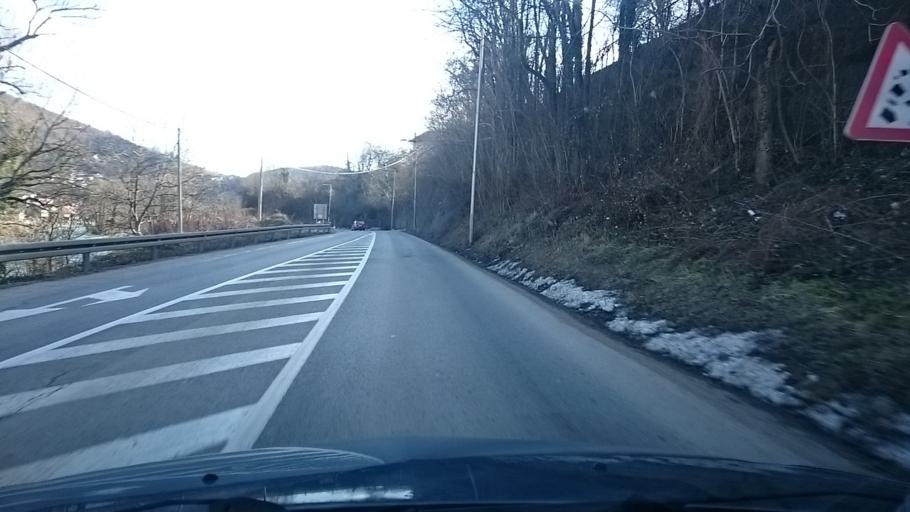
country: BA
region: Republika Srpska
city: Hiseti
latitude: 44.7420
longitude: 17.1528
